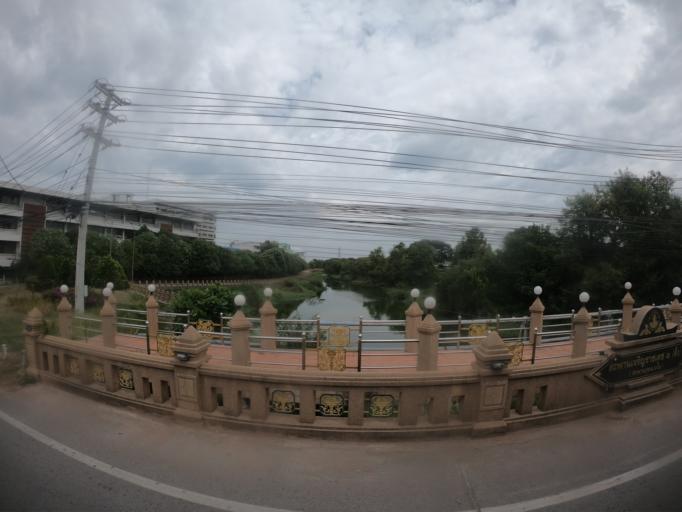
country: TH
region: Maha Sarakham
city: Maha Sarakham
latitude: 16.1779
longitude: 103.3128
